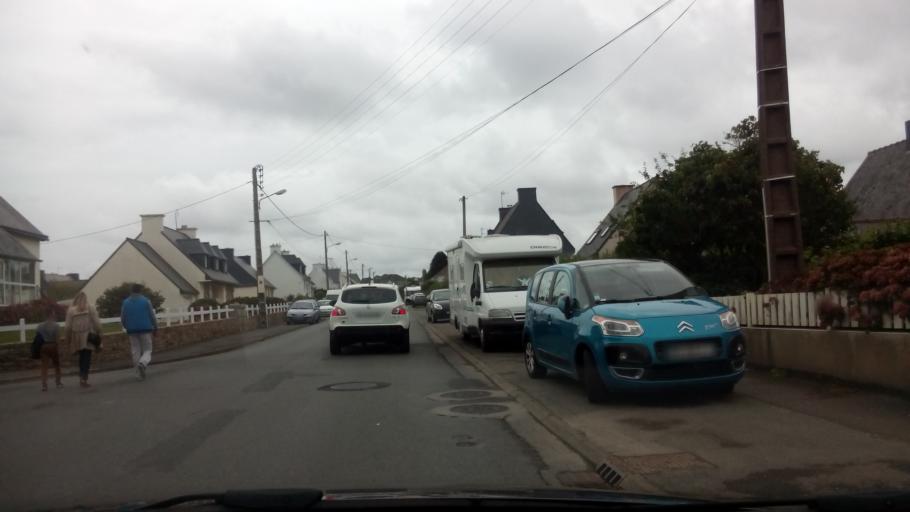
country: FR
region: Brittany
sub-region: Departement des Cotes-d'Armor
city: Plestin-les-Greves
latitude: 48.6666
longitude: -3.6329
